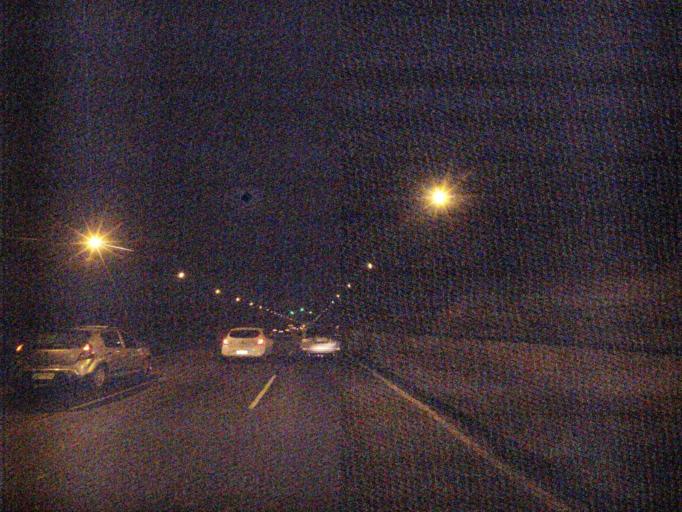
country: BR
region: Rio de Janeiro
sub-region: Rio De Janeiro
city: Rio de Janeiro
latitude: -22.9539
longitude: -43.2052
